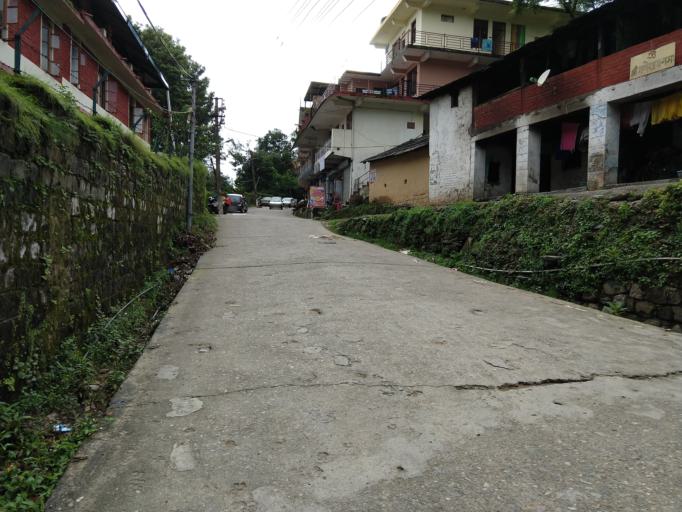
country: IN
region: Himachal Pradesh
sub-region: Kangra
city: Dharmsala
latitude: 32.2215
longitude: 76.3283
